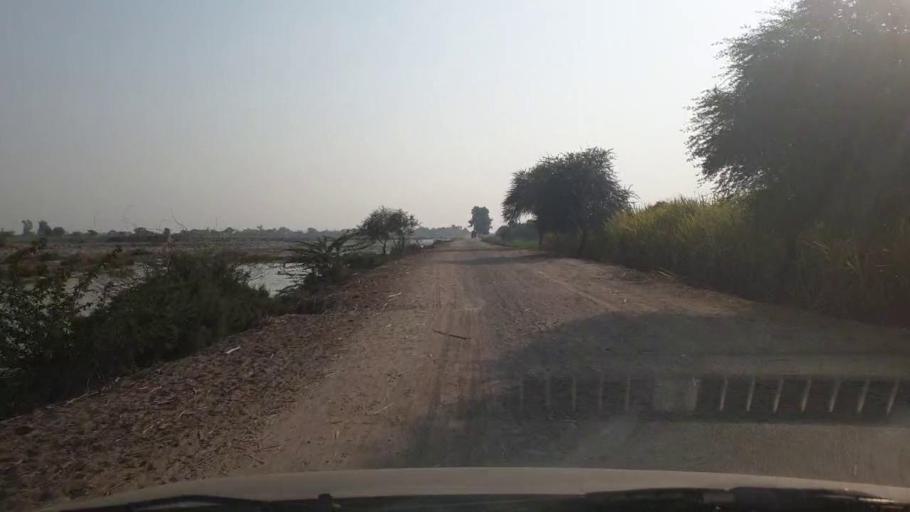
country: PK
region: Sindh
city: Digri
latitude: 25.2585
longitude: 69.1626
